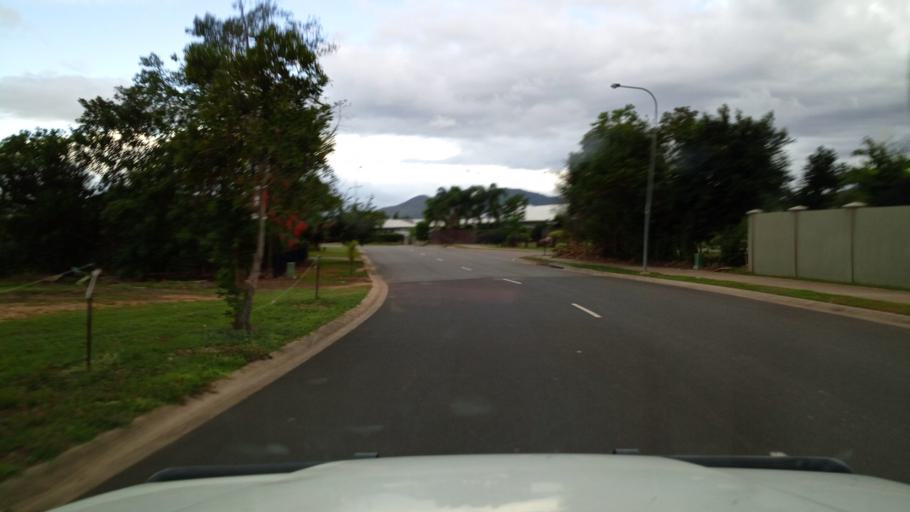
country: AU
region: Queensland
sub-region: Cairns
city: Redlynch
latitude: -16.8416
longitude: 145.6905
